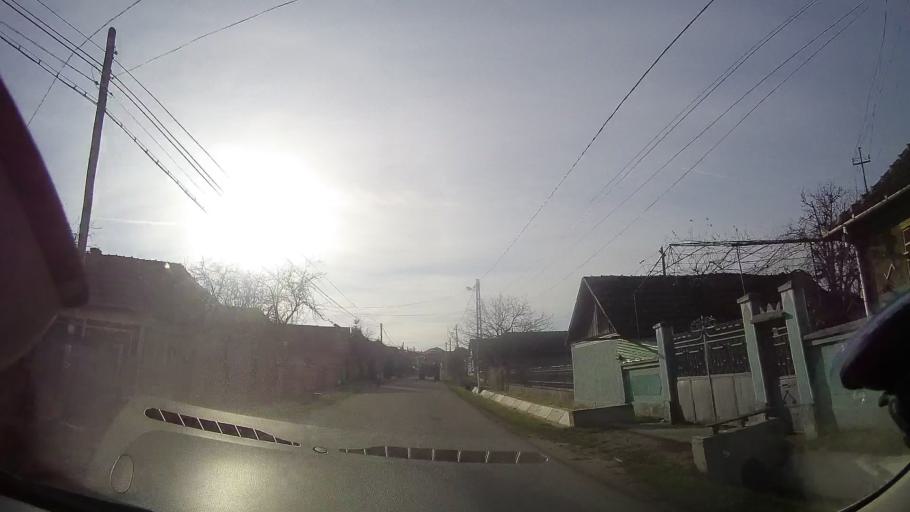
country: RO
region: Bihor
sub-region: Comuna Sarbi
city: Sarbi
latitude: 47.1962
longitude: 22.1226
